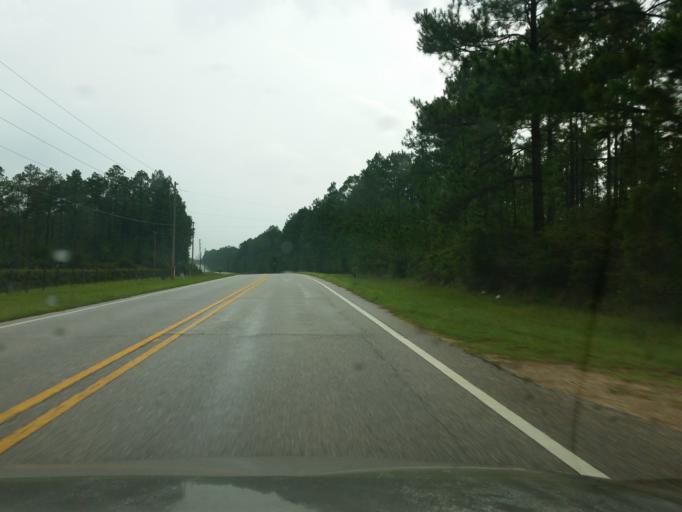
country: US
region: Alabama
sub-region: Baldwin County
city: Elberta
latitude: 30.5241
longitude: -87.4973
